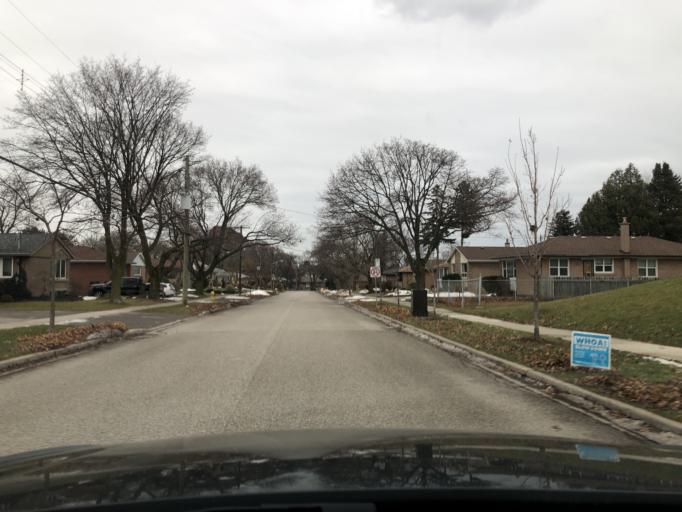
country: CA
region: Ontario
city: Etobicoke
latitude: 43.6947
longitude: -79.5381
